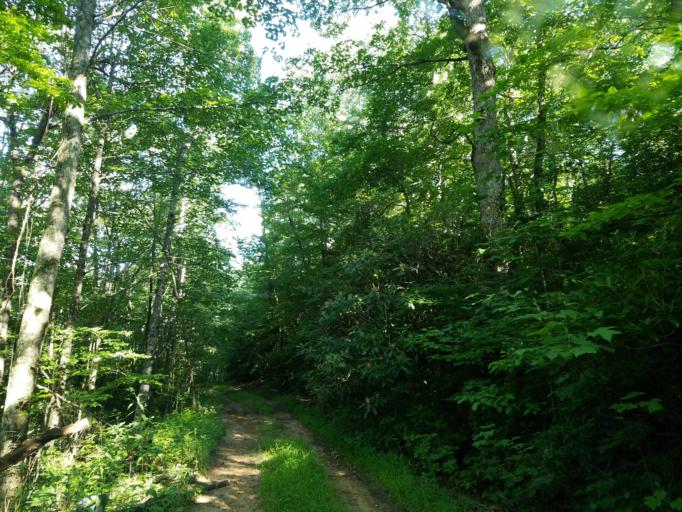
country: US
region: Georgia
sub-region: Dawson County
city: Dawsonville
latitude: 34.6156
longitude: -84.2283
